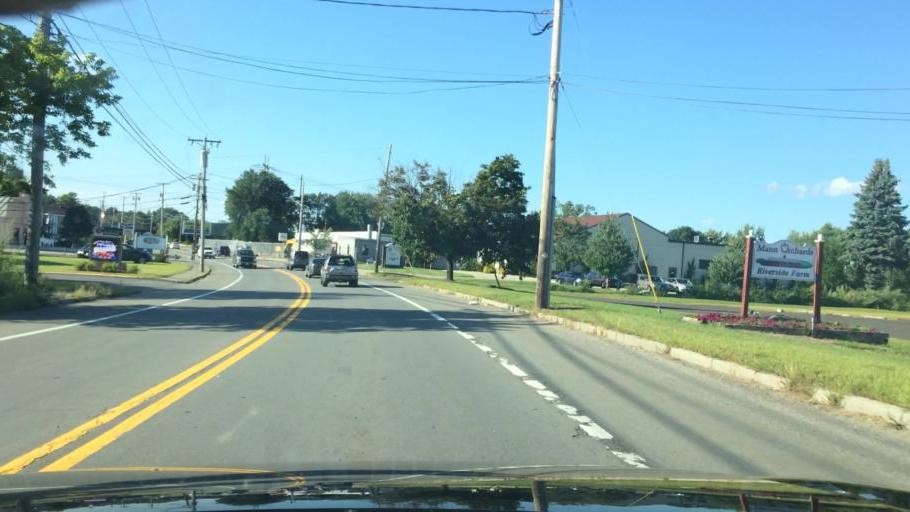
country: US
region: Massachusetts
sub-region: Essex County
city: North Andover
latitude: 42.7500
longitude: -71.1270
